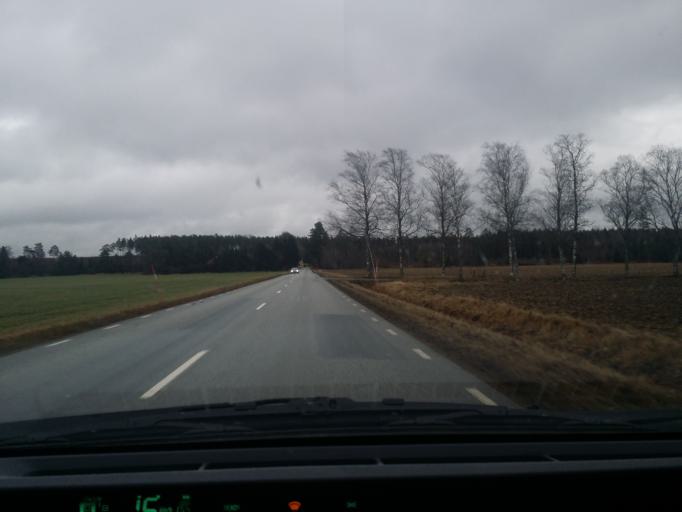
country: SE
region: Vaestmanland
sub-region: Sala Kommun
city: Sala
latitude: 59.8103
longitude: 16.5329
